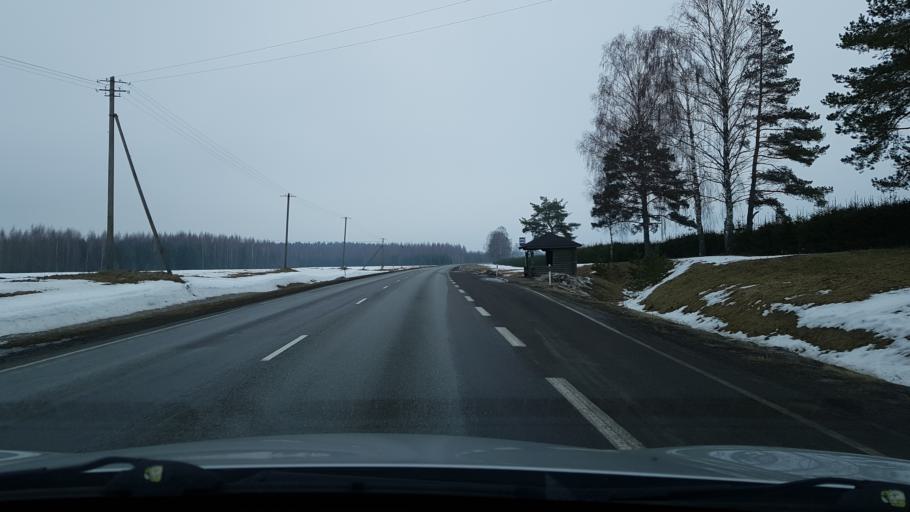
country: EE
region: Valgamaa
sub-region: Valga linn
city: Valga
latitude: 57.8988
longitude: 26.1685
